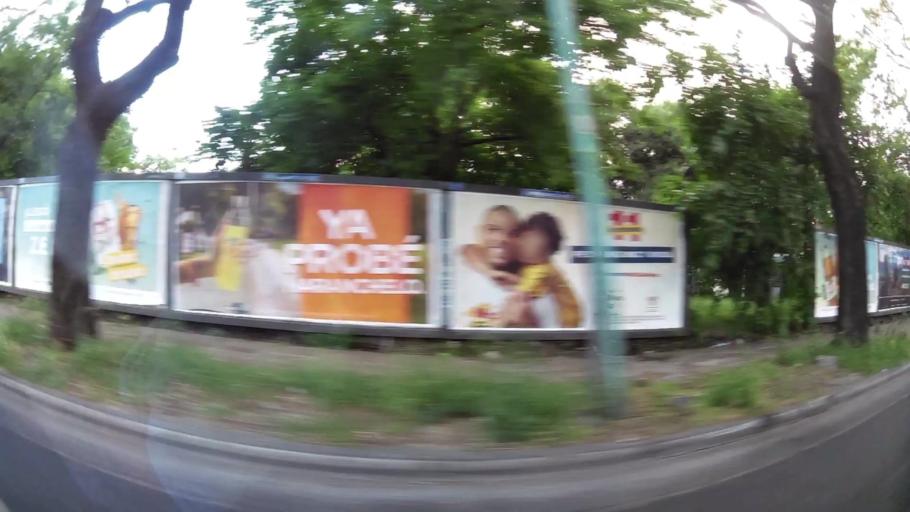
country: AR
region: Buenos Aires
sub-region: Partido de General San Martin
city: General San Martin
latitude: -34.5772
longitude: -58.5124
